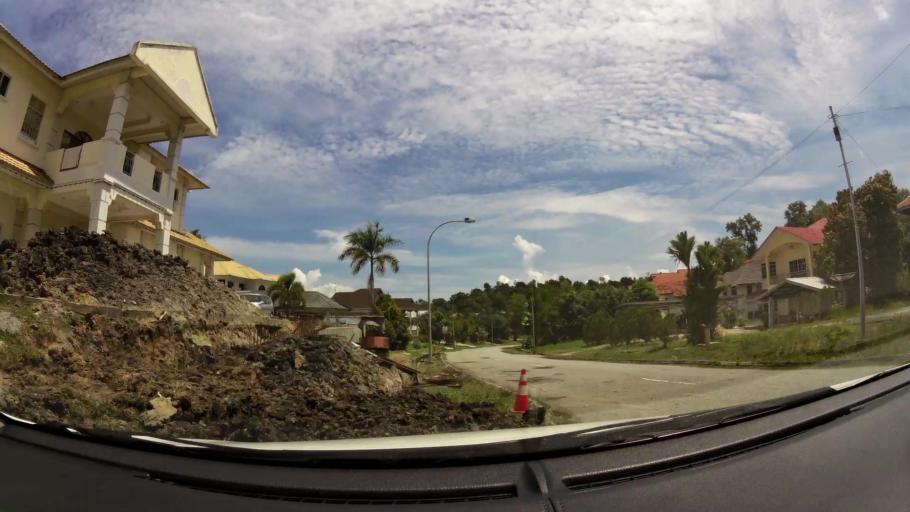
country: BN
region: Brunei and Muara
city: Bandar Seri Begawan
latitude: 4.9621
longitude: 114.9072
